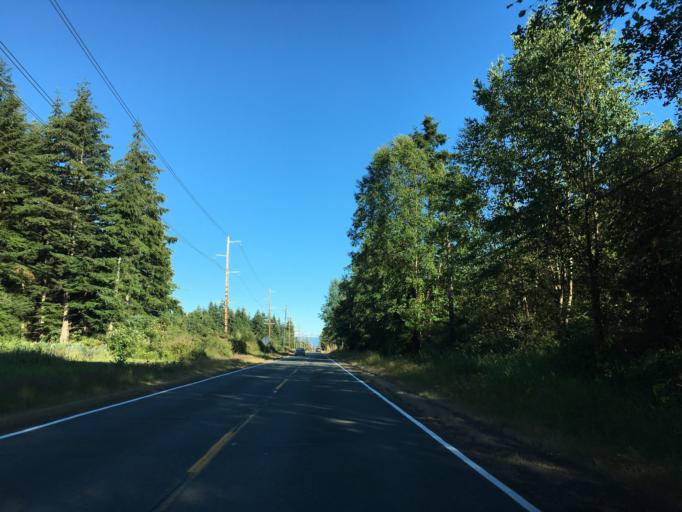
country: US
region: Washington
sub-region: Whatcom County
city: Birch Bay
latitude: 48.9332
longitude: -122.6643
